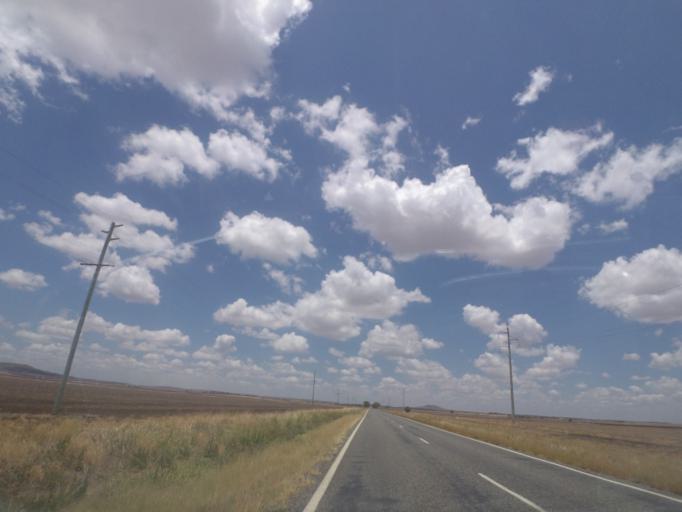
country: AU
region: Queensland
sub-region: Toowoomba
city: Top Camp
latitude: -27.9092
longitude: 151.9790
